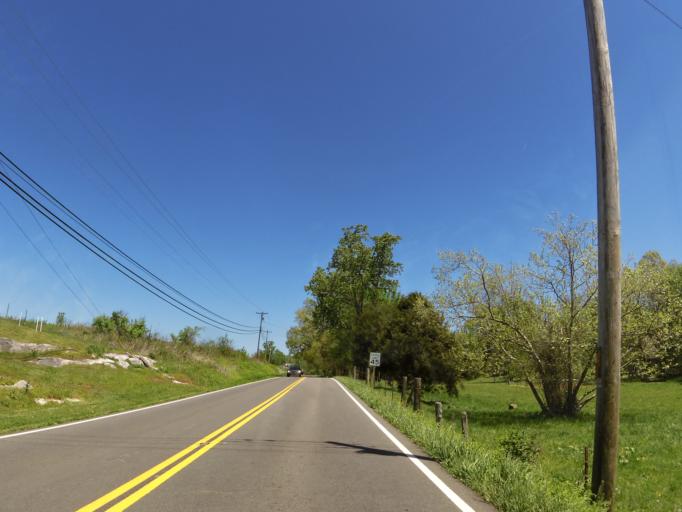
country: US
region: Tennessee
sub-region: Greene County
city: Mosheim
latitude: 36.1060
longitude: -82.9202
